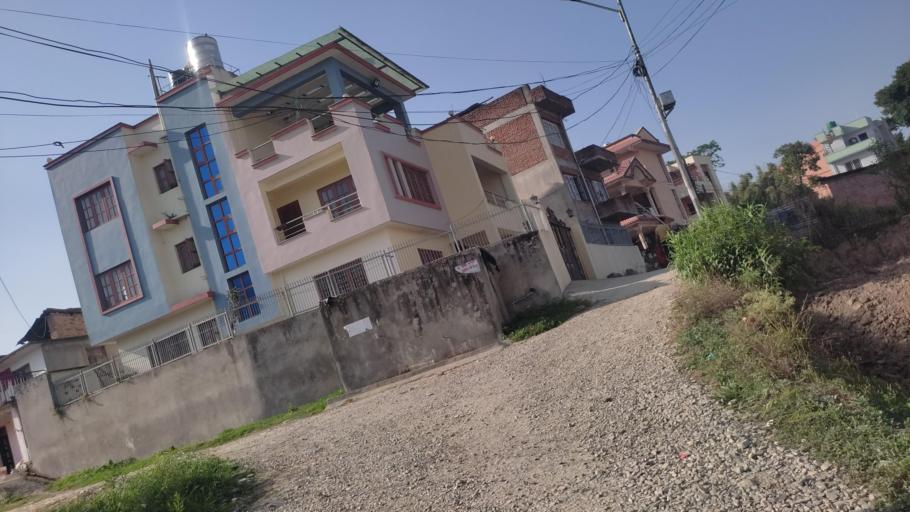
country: NP
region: Central Region
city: Kirtipur
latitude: 27.6563
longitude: 85.2846
